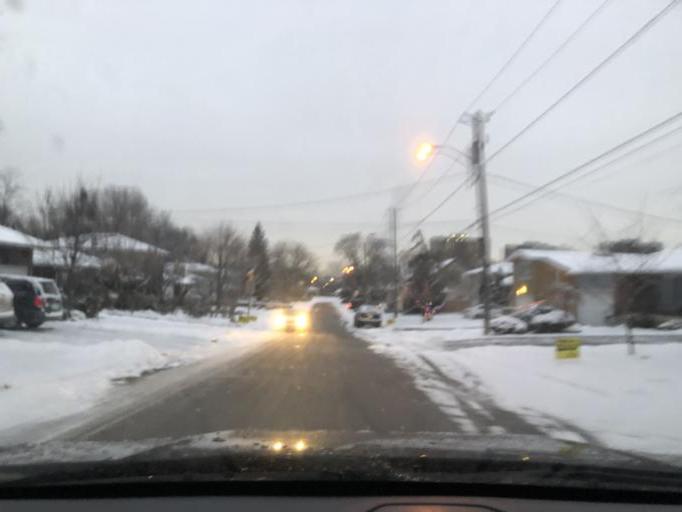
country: CA
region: Ontario
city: Toronto
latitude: 43.6970
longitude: -79.4808
